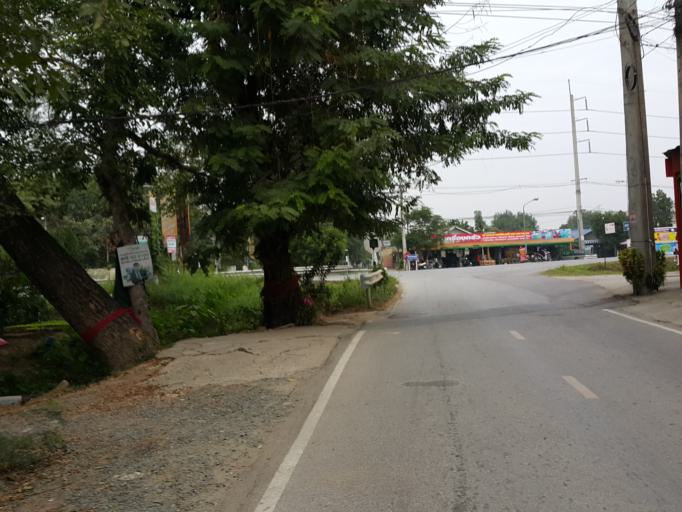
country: TH
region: Chiang Mai
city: Saraphi
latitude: 18.7462
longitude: 99.0516
